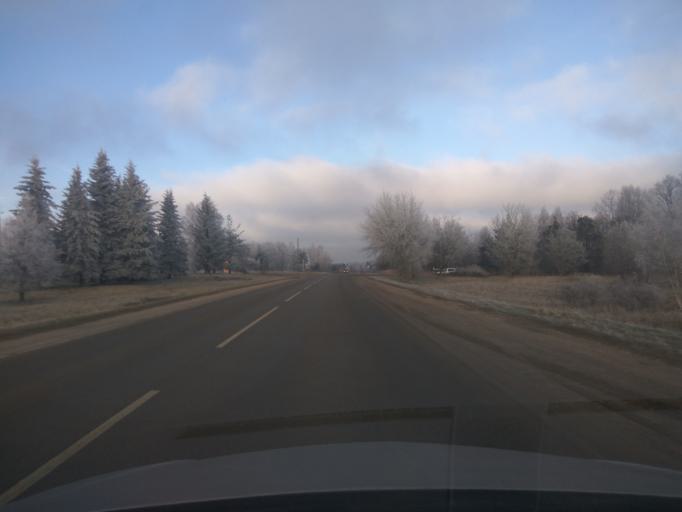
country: LV
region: Kuldigas Rajons
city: Kuldiga
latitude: 56.9690
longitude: 21.9336
